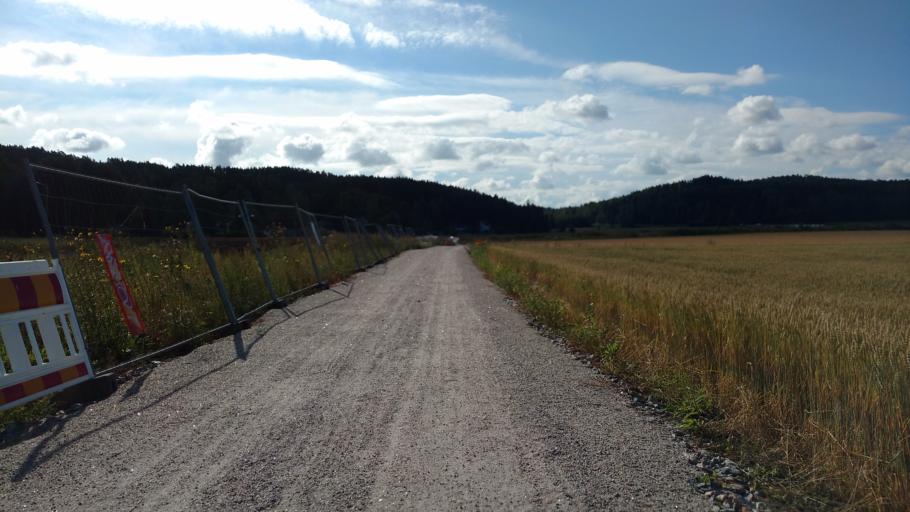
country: FI
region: Varsinais-Suomi
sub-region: Salo
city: Salo
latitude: 60.3746
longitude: 23.1671
